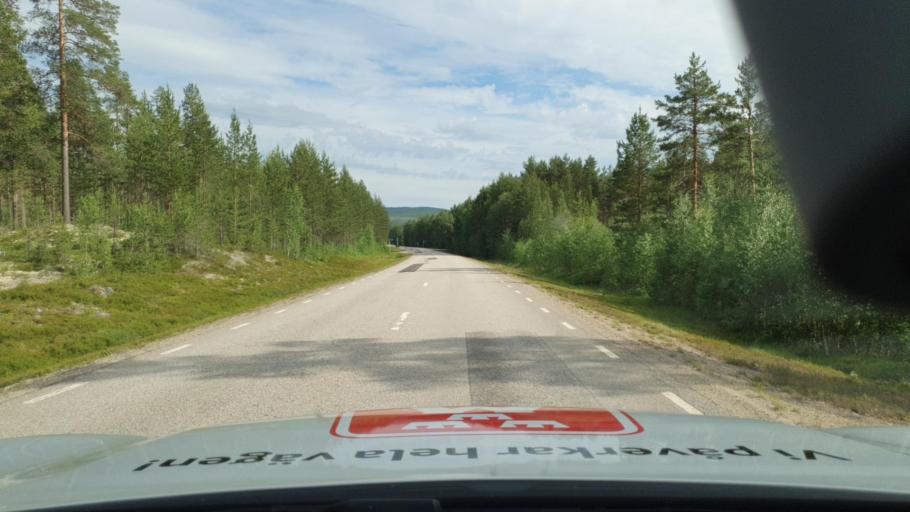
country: NO
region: Hedmark
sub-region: Trysil
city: Innbygda
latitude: 60.9454
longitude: 12.4709
